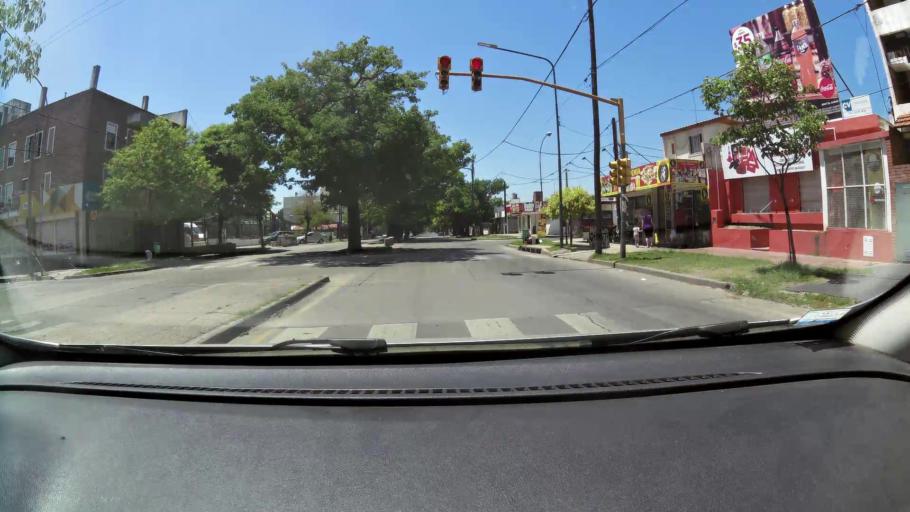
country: AR
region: Cordoba
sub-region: Departamento de Capital
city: Cordoba
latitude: -31.4084
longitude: -64.2194
